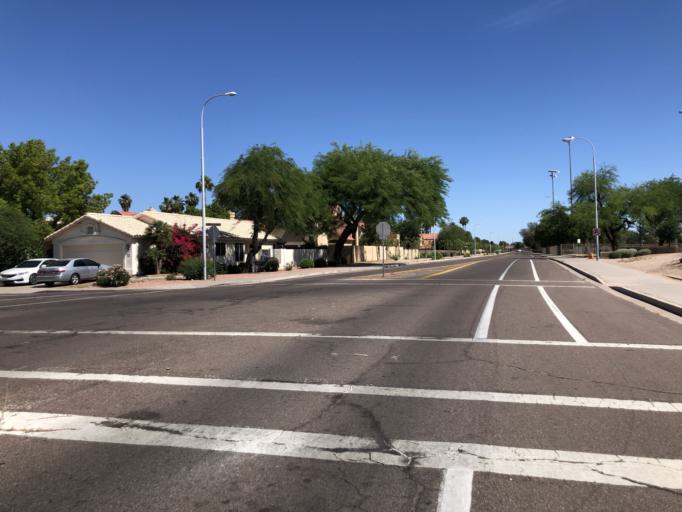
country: US
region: Arizona
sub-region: Maricopa County
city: Guadalupe
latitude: 33.3158
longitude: -111.9196
